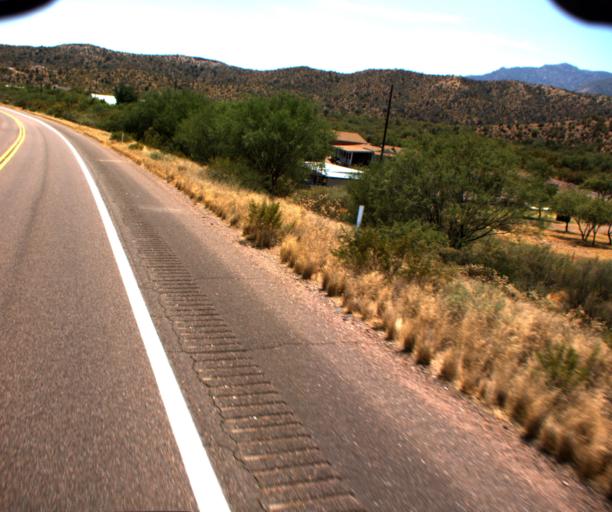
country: US
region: Arizona
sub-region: Gila County
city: Tonto Basin
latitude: 33.9615
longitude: -111.3258
